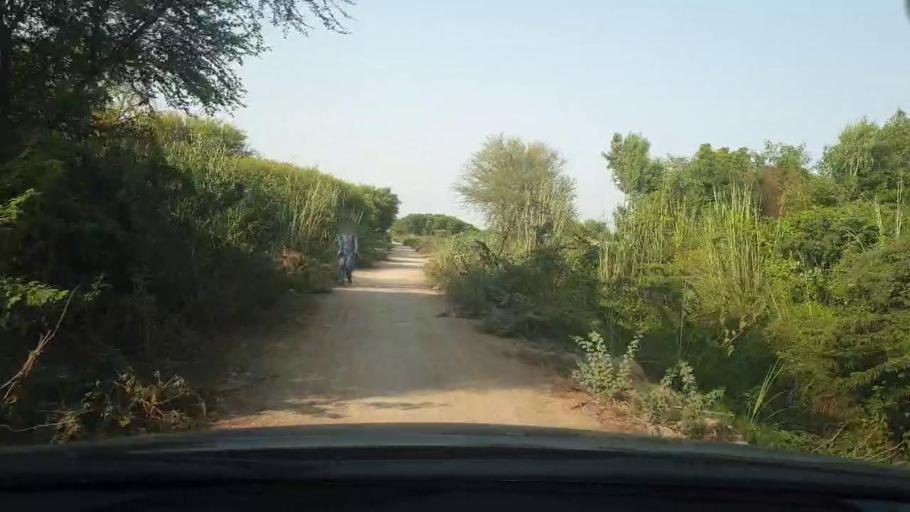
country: PK
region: Sindh
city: Naukot
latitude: 24.7824
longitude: 69.2347
